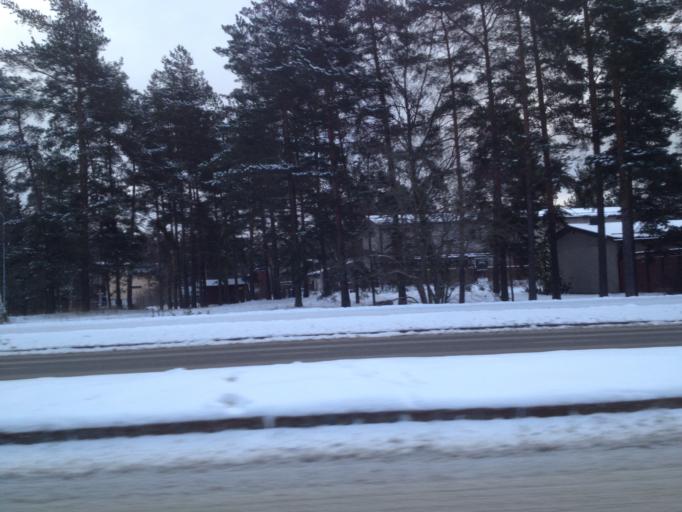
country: FI
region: Uusimaa
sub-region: Helsinki
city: Vantaa
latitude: 60.2088
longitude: 25.1487
